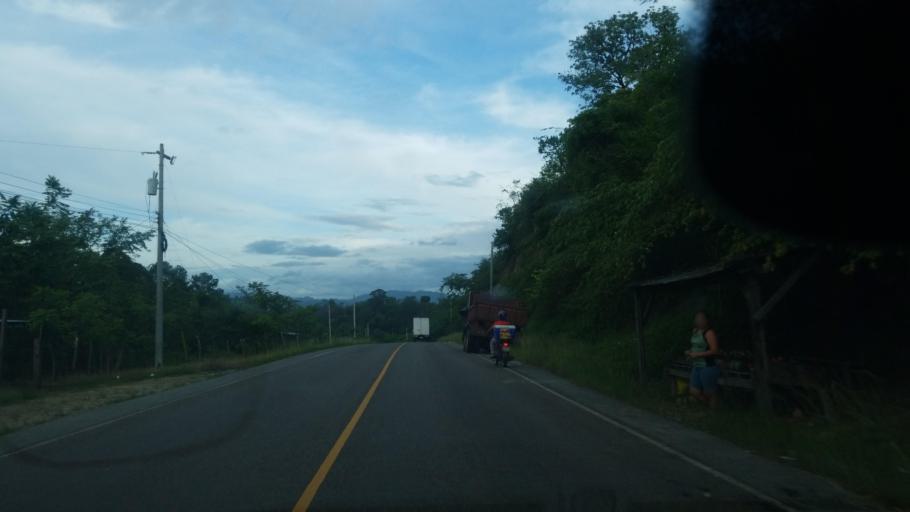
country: HN
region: Santa Barbara
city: Concepcion del Sur
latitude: 14.7967
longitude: -88.1669
